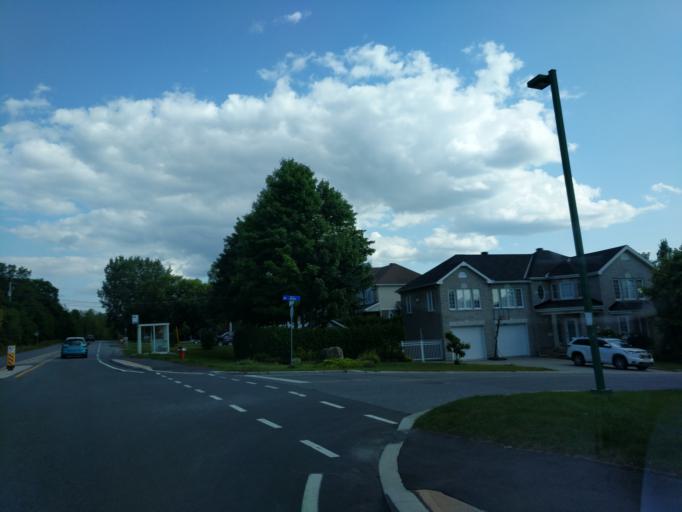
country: CA
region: Quebec
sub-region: Outaouais
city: Gatineau
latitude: 45.4482
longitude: -75.7828
